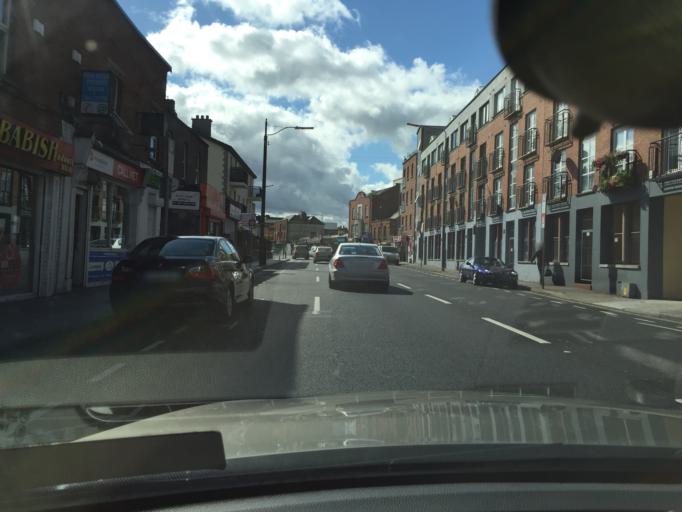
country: IE
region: Leinster
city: Rathmines
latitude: 53.3337
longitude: -6.2750
